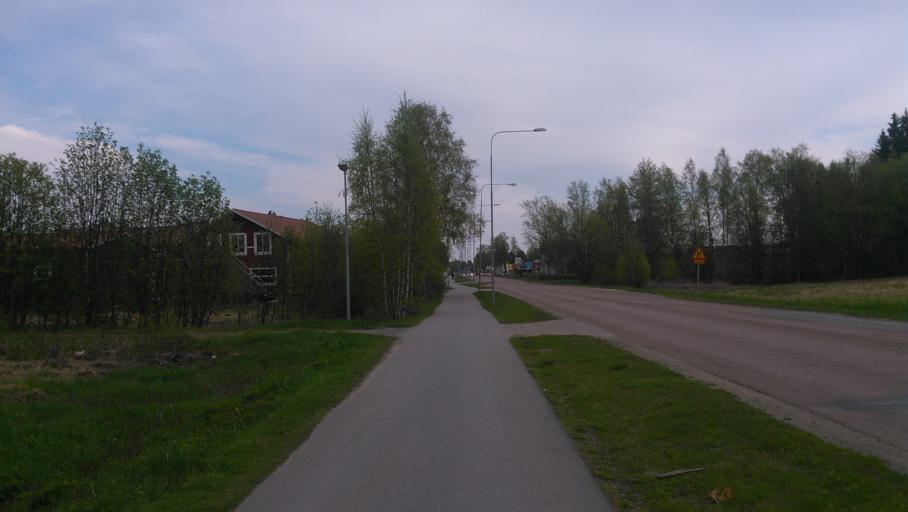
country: SE
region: Vaesterbotten
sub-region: Umea Kommun
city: Umea
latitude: 63.8087
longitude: 20.2712
